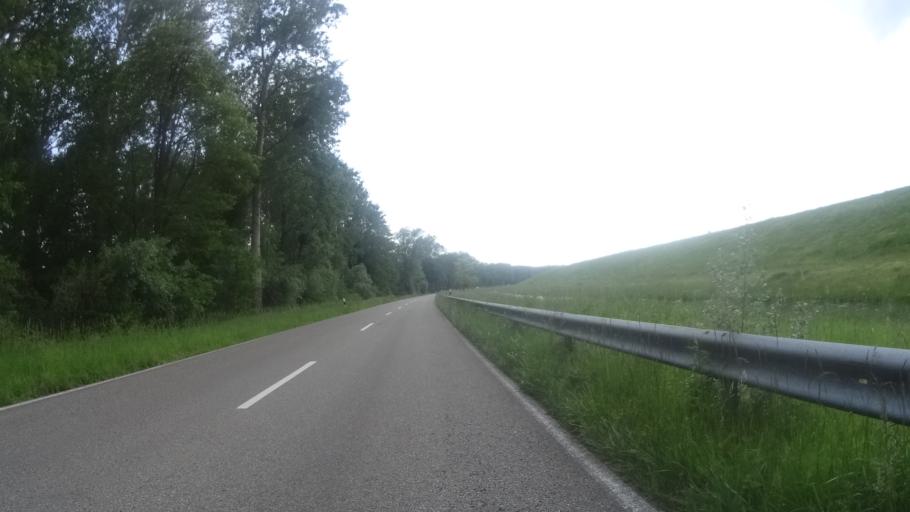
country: DE
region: Baden-Wuerttemberg
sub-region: Karlsruhe Region
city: Hugelsheim
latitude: 48.7912
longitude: 8.0748
